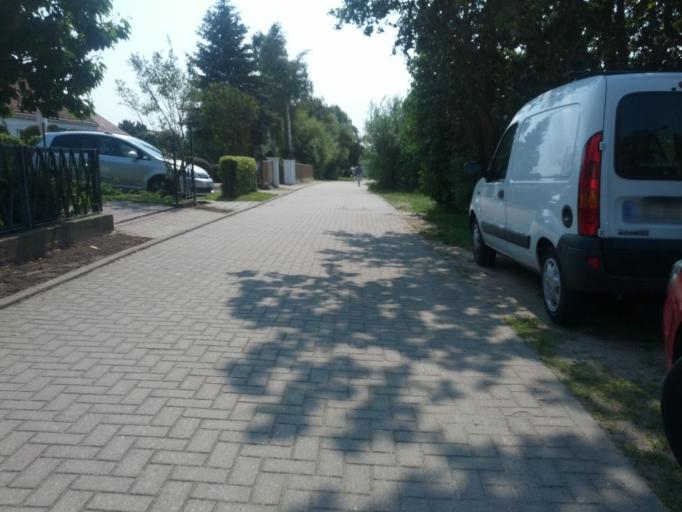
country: DE
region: Mecklenburg-Vorpommern
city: Bastorf
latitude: 54.1015
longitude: 11.6156
